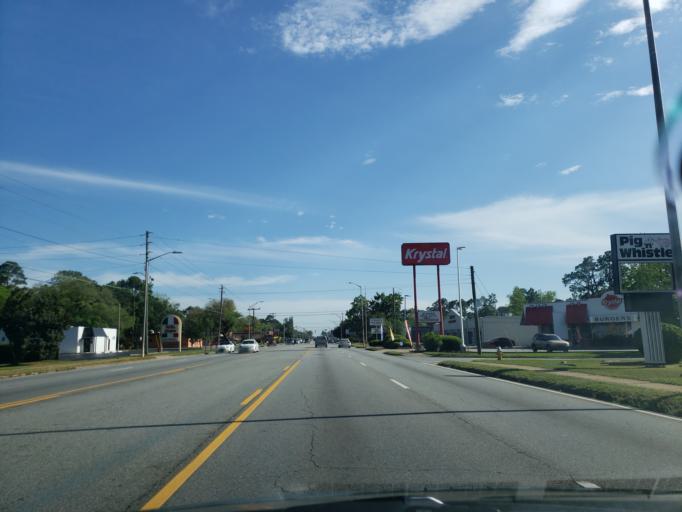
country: US
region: Georgia
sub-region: Dougherty County
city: Albany
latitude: 31.5996
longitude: -84.1760
